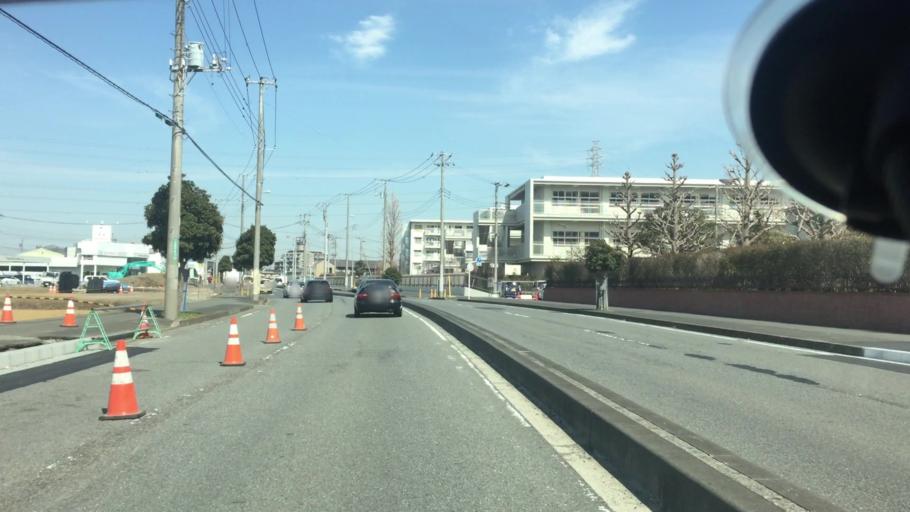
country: JP
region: Kanagawa
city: Atsugi
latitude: 35.4322
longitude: 139.3833
